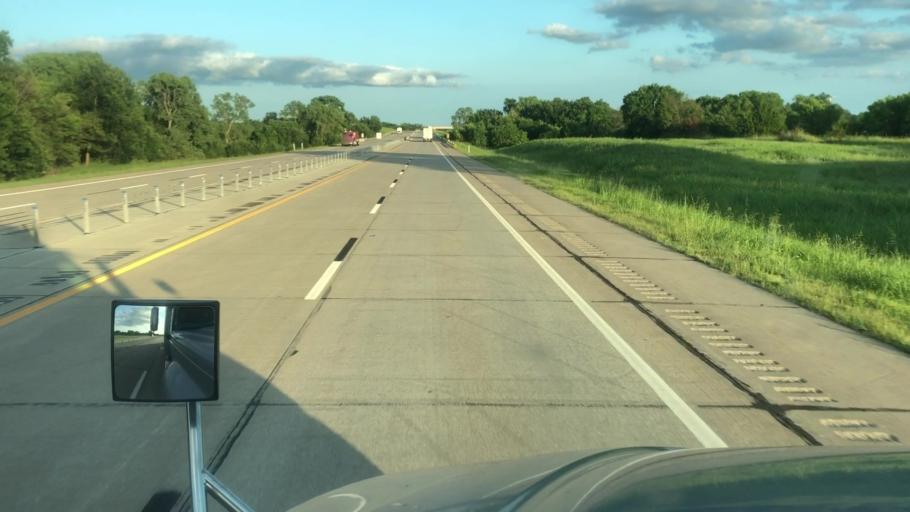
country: US
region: Oklahoma
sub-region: Pawnee County
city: Pawnee
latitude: 36.3262
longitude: -97.0056
